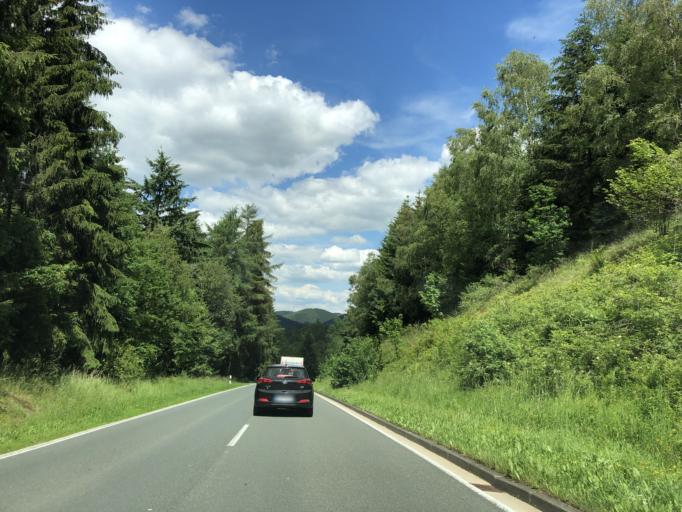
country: DE
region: North Rhine-Westphalia
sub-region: Regierungsbezirk Arnsberg
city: Kirchhundem
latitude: 51.1063
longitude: 8.1360
